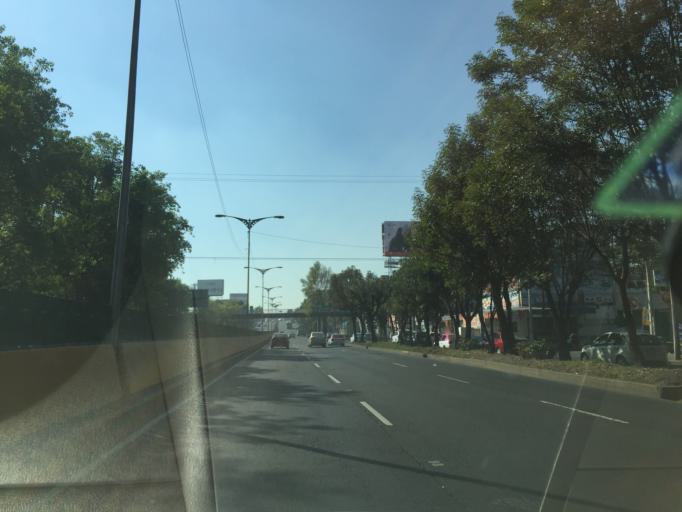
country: MX
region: Mexico City
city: Azcapotzalco
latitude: 19.4664
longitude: -99.1899
